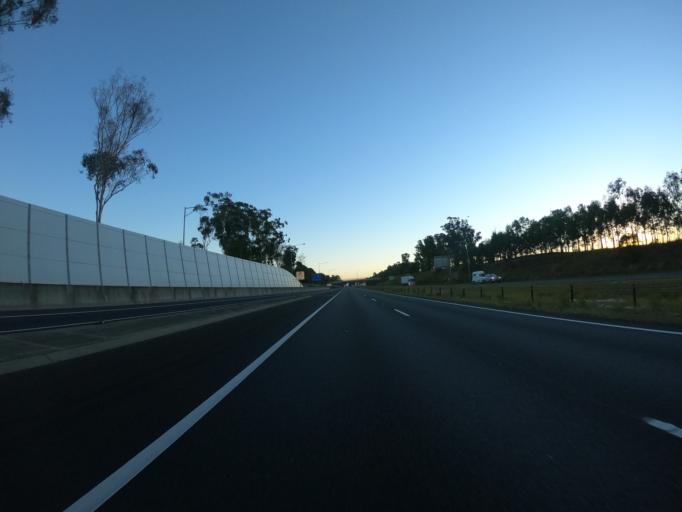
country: AU
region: New South Wales
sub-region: Blacktown
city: Glendenning
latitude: -33.7486
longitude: 150.8458
